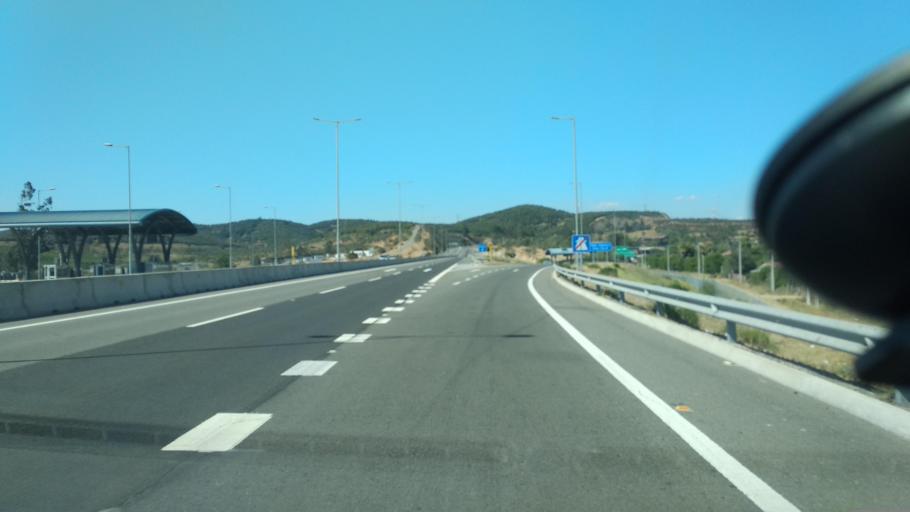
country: CL
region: Valparaiso
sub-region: Provincia de Marga Marga
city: Limache
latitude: -32.9741
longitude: -71.3028
